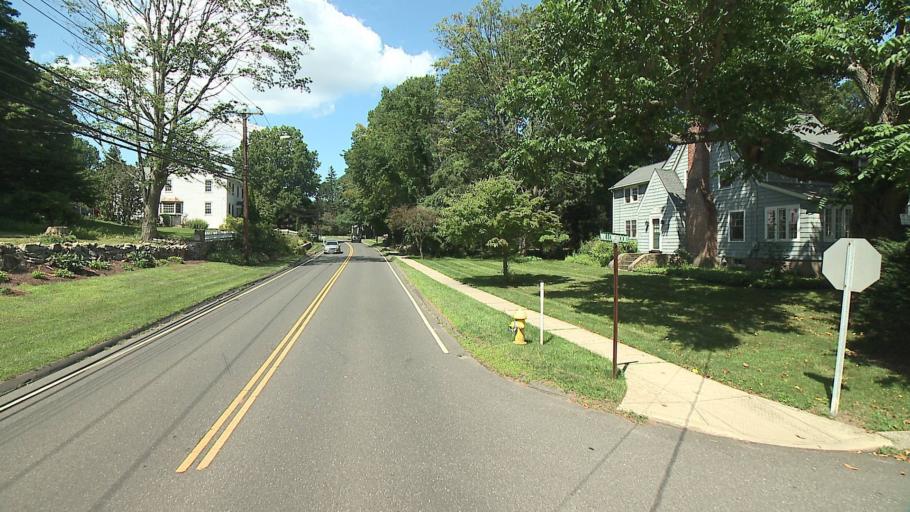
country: US
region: Connecticut
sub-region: Fairfield County
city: Trumbull
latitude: 41.2496
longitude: -73.1625
